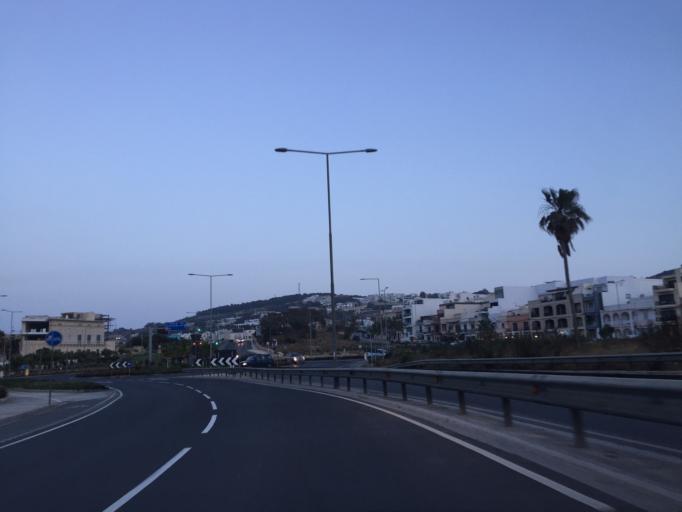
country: MT
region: Hal Gharghur
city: Hal Gharghur
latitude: 35.9403
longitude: 14.4548
